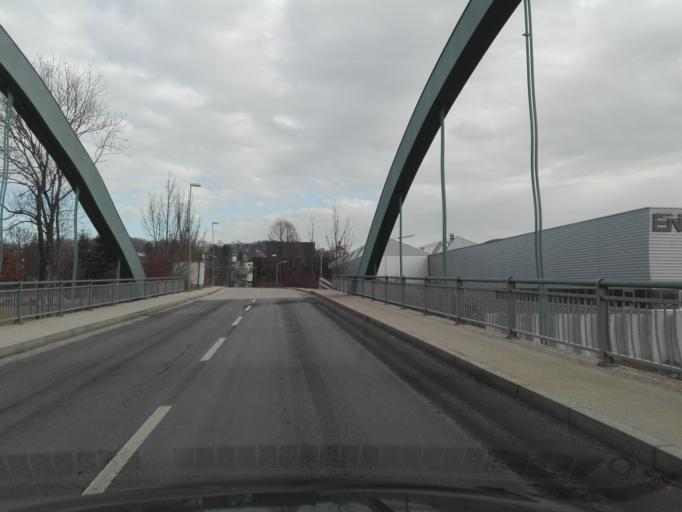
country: AT
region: Upper Austria
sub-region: Politischer Bezirk Perg
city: Perg
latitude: 48.2706
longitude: 14.5775
